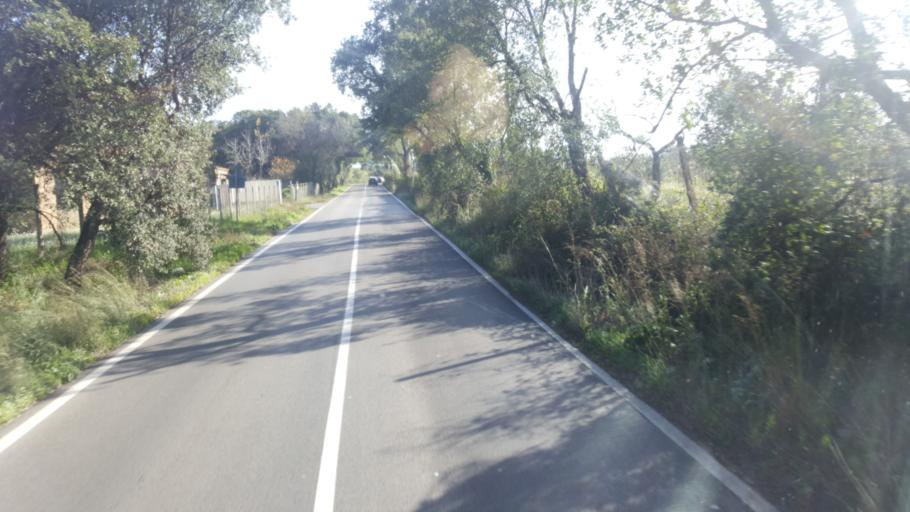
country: IT
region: Latium
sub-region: Citta metropolitana di Roma Capitale
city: Mantiglia di Ardea
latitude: 41.6873
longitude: 12.6083
